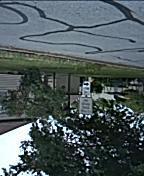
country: US
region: Kentucky
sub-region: Jefferson County
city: Middletown
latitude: 38.2456
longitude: -85.5299
